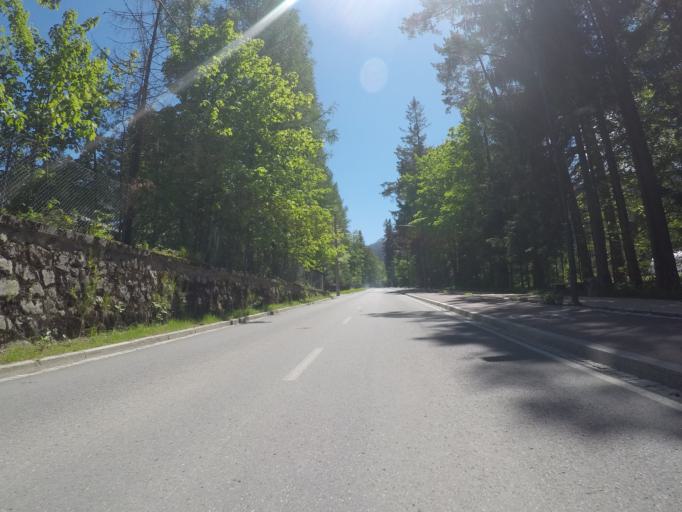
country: PL
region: Lesser Poland Voivodeship
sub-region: Powiat tatrzanski
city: Zakopane
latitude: 49.2834
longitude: 19.9753
